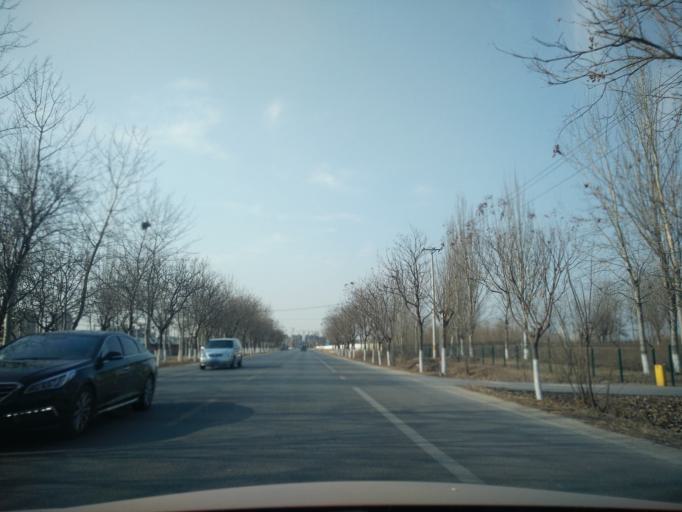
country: CN
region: Beijing
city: Yinghai
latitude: 39.7650
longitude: 116.4586
